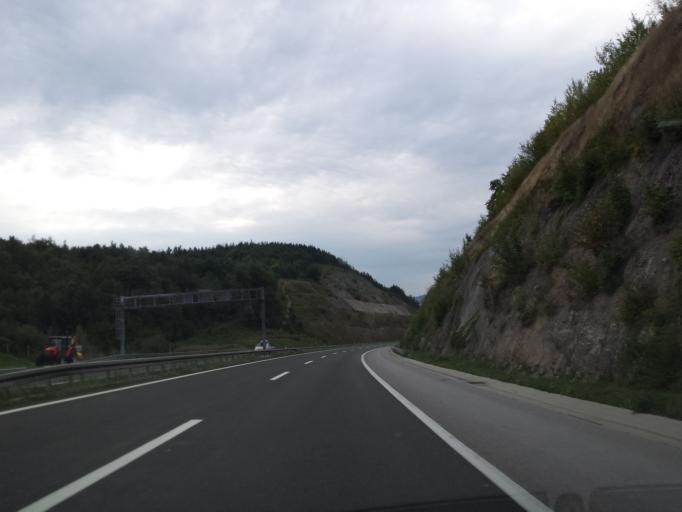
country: HR
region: Karlovacka
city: Ostarije
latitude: 45.1484
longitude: 15.2737
